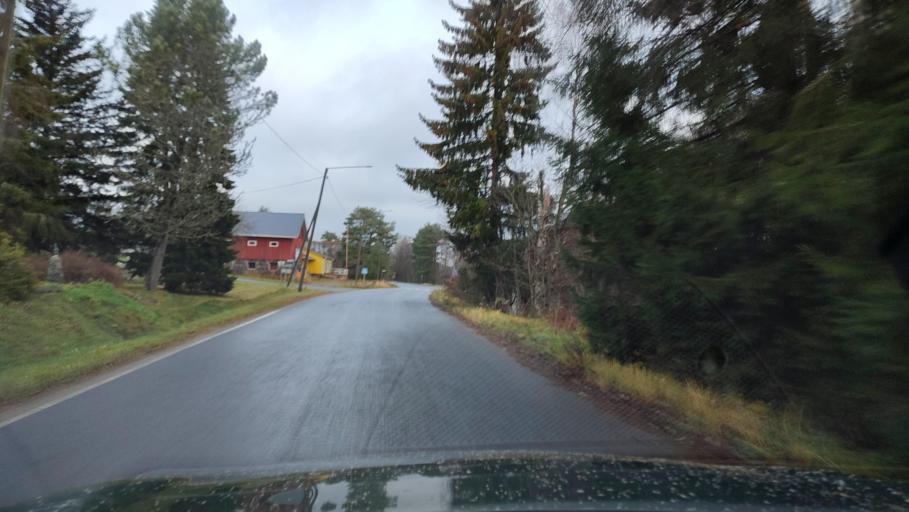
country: FI
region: Southern Ostrobothnia
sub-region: Suupohja
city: Karijoki
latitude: 62.3796
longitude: 21.5559
